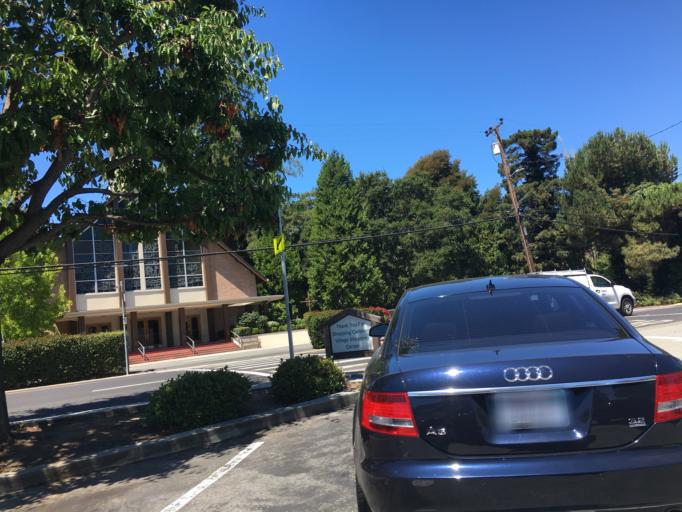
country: US
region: California
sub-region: San Mateo County
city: Belmont
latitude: 37.5109
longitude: -122.2936
